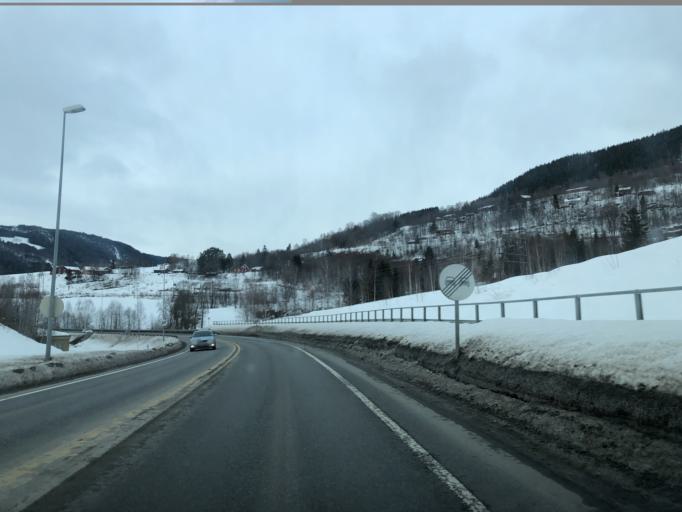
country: NO
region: Oppland
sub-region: Lillehammer
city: Lillehammer
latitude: 61.1504
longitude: 10.4128
